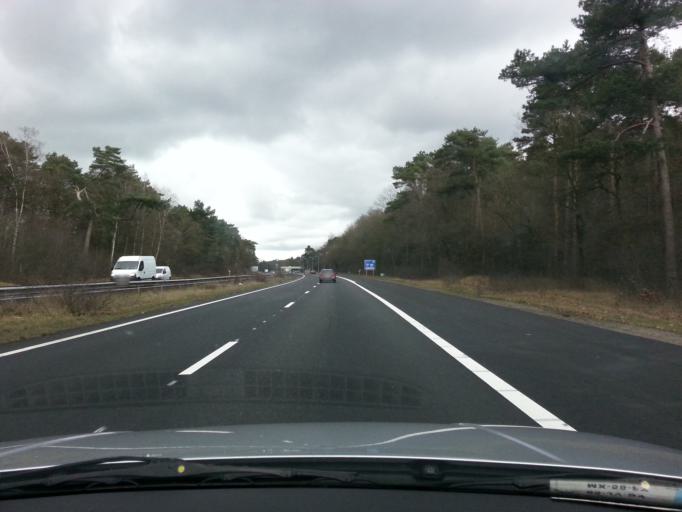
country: NL
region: Gelderland
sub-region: Gemeente Oldebroek
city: Oldebroek
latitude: 52.4457
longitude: 5.9732
